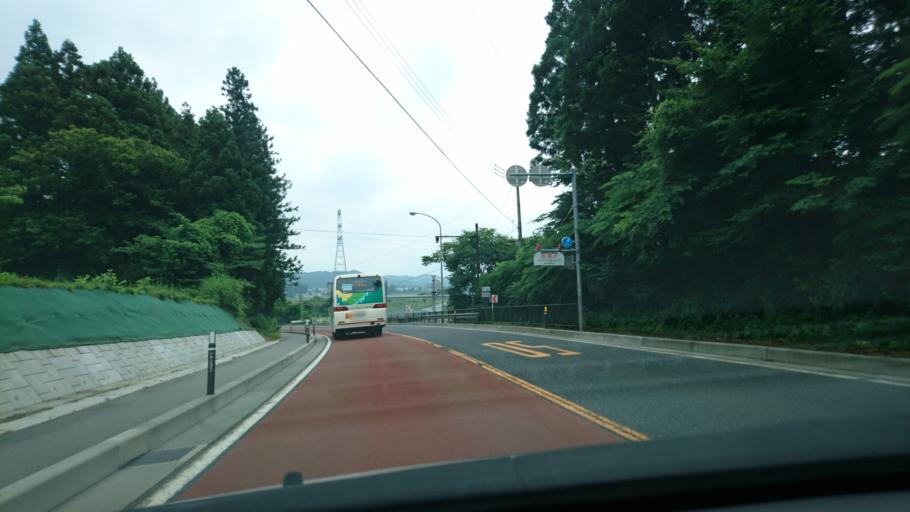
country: JP
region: Miyagi
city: Furukawa
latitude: 38.7160
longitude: 140.8171
